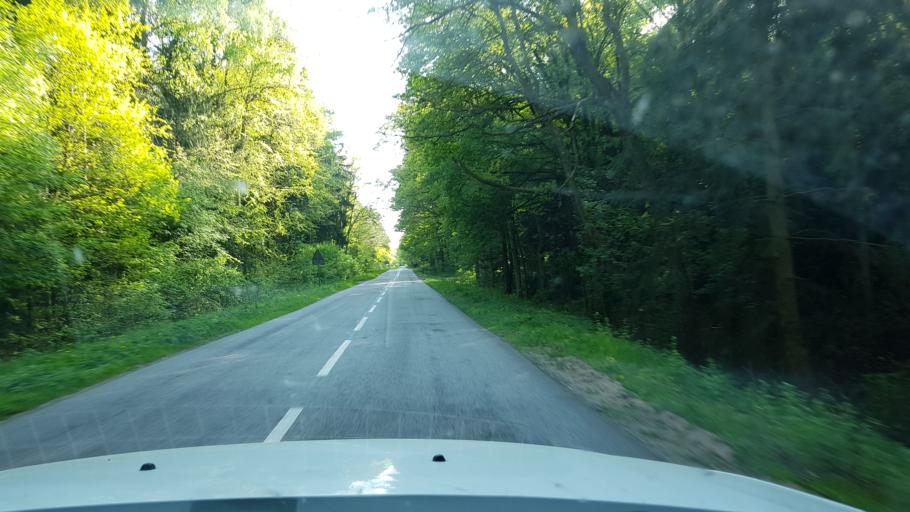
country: PL
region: West Pomeranian Voivodeship
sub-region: Powiat lobeski
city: Resko
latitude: 53.7301
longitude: 15.3276
